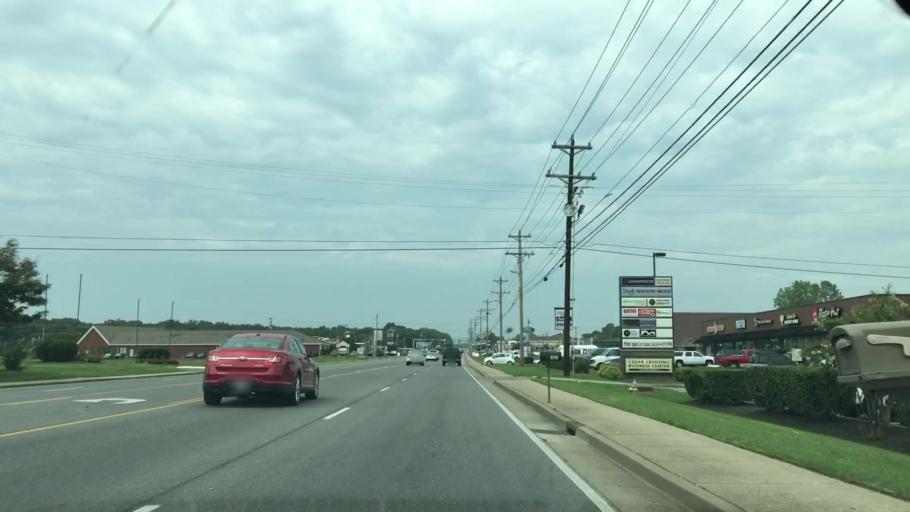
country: US
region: Tennessee
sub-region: Wilson County
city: Lebanon
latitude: 36.2201
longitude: -86.3409
